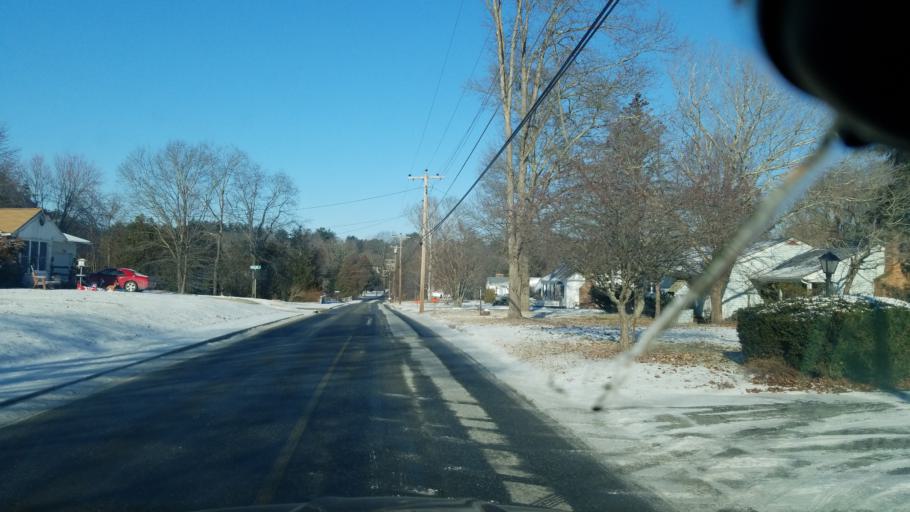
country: US
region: Connecticut
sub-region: Windham County
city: East Brooklyn
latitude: 41.8024
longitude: -71.9007
